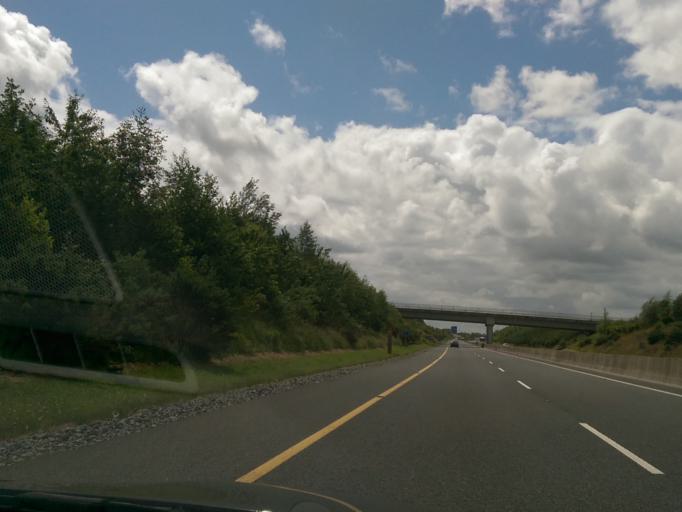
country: IE
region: Munster
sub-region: County Cork
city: Mitchelstown
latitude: 52.2899
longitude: -8.2041
